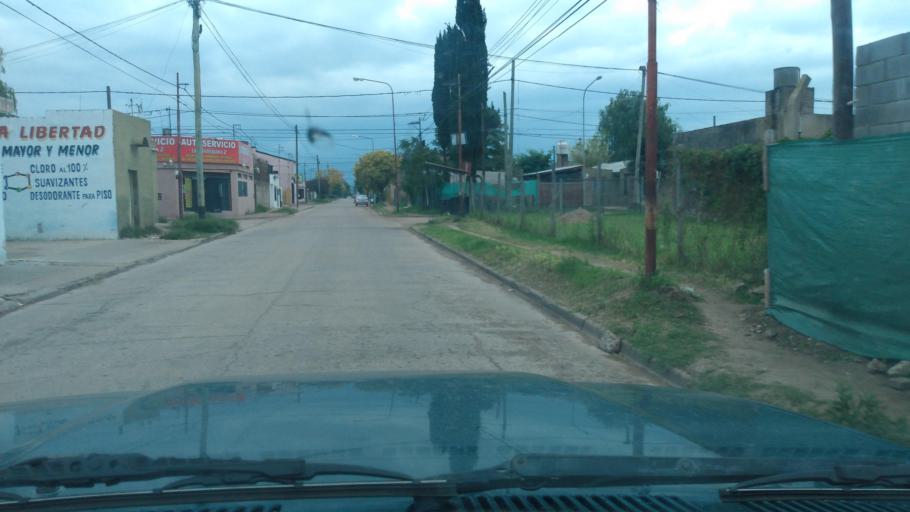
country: AR
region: Buenos Aires
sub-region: Partido de Lujan
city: Lujan
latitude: -34.5626
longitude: -59.0904
